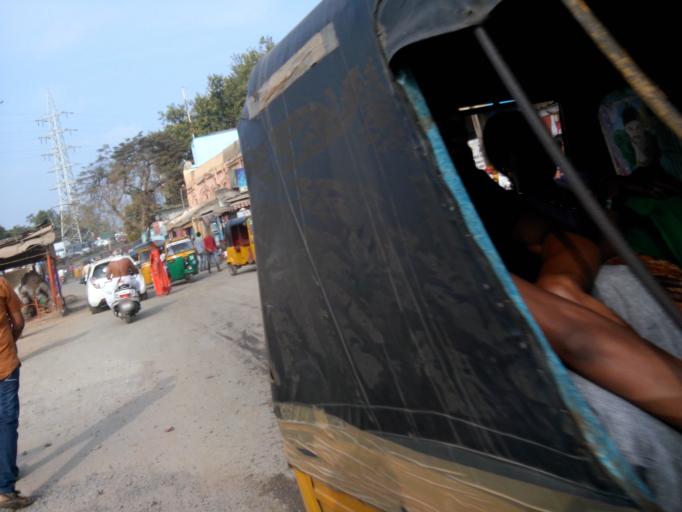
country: IN
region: Andhra Pradesh
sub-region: Krishna
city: Vijayawada
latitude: 16.5124
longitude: 80.6077
